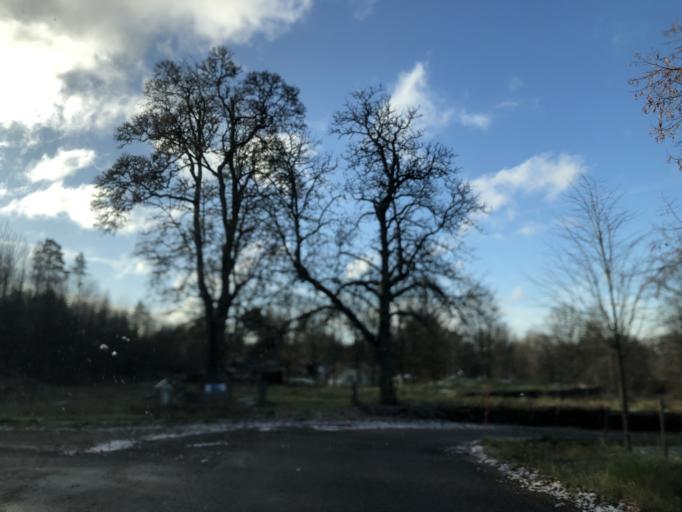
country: SE
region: Vaestra Goetaland
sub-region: Ulricehamns Kommun
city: Ulricehamn
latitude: 57.7202
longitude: 13.4032
